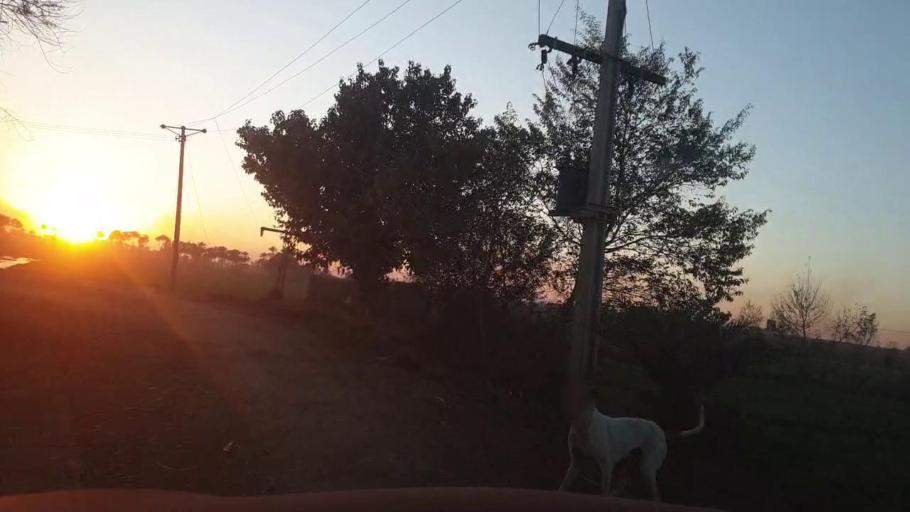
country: PK
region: Sindh
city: Ghotki
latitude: 28.0580
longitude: 69.3588
